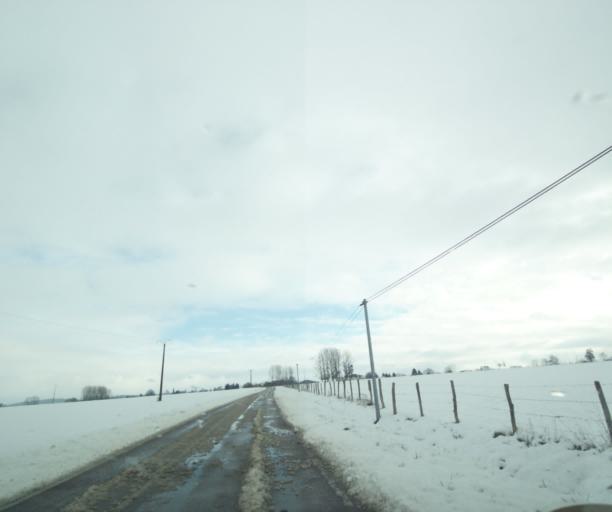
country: FR
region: Champagne-Ardenne
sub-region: Departement de la Haute-Marne
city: Montier-en-Der
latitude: 48.4542
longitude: 4.6651
